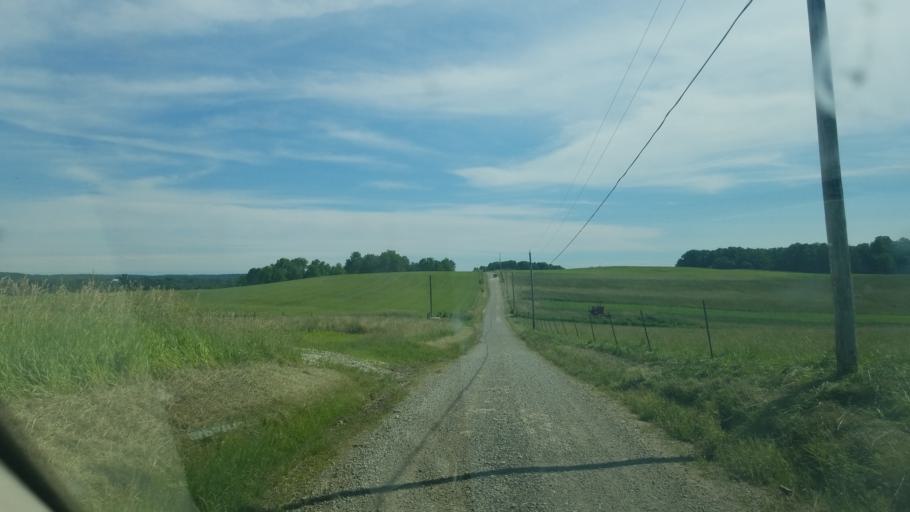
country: US
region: Ohio
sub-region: Holmes County
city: Millersburg
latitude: 40.4774
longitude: -81.9631
